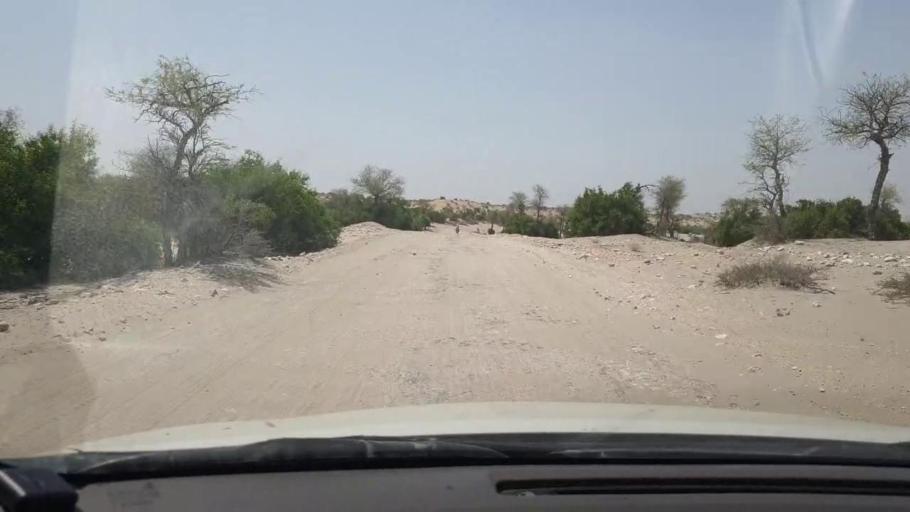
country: PK
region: Sindh
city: Rohri
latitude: 27.3067
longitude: 69.2815
